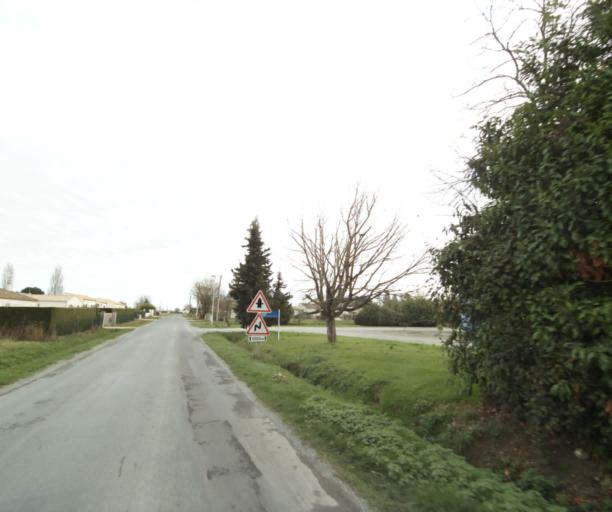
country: FR
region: Poitou-Charentes
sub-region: Departement de la Charente-Maritime
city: Corme-Royal
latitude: 45.7442
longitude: -0.8079
